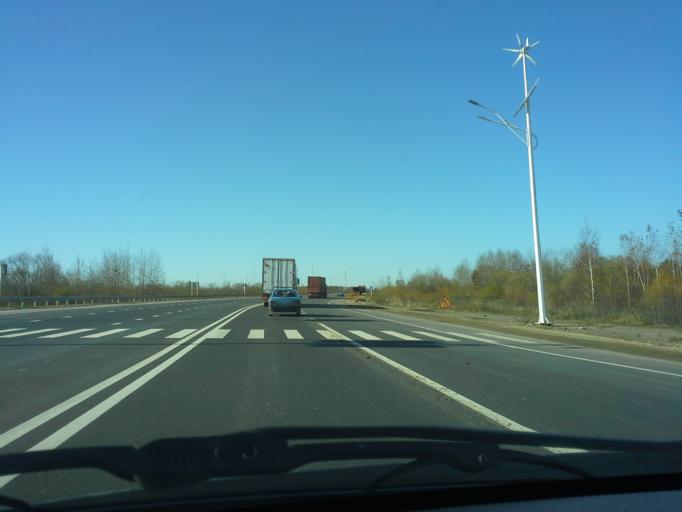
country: RU
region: Jewish Autonomous Oblast
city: Priamurskiy
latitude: 48.5174
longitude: 134.9100
